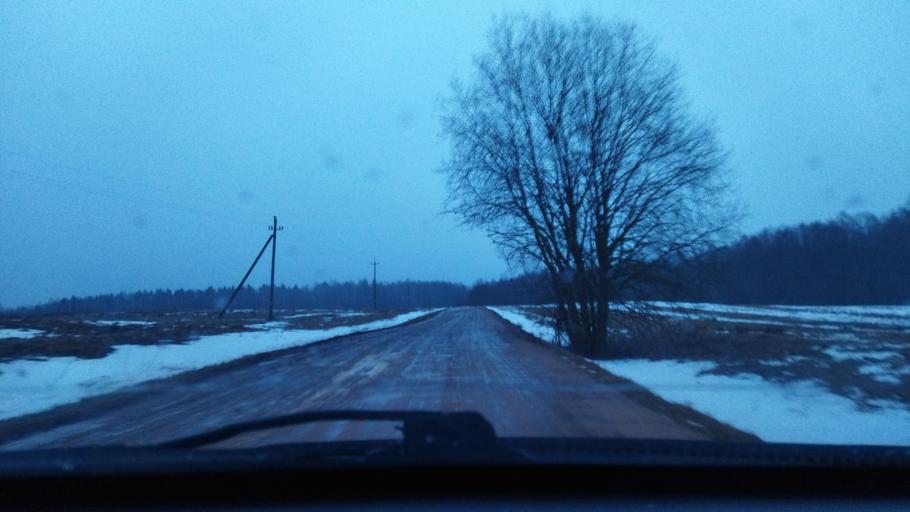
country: BY
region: Minsk
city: Svir
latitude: 54.9357
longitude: 26.3854
